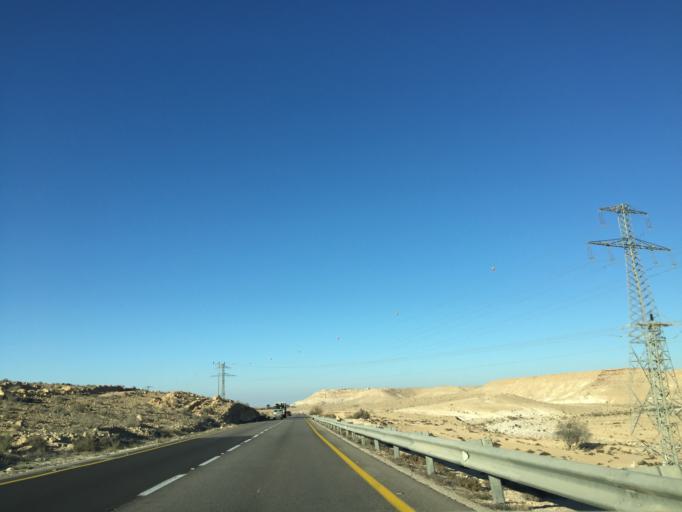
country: IL
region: Southern District
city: Midreshet Ben-Gurion
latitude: 30.7681
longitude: 34.7719
